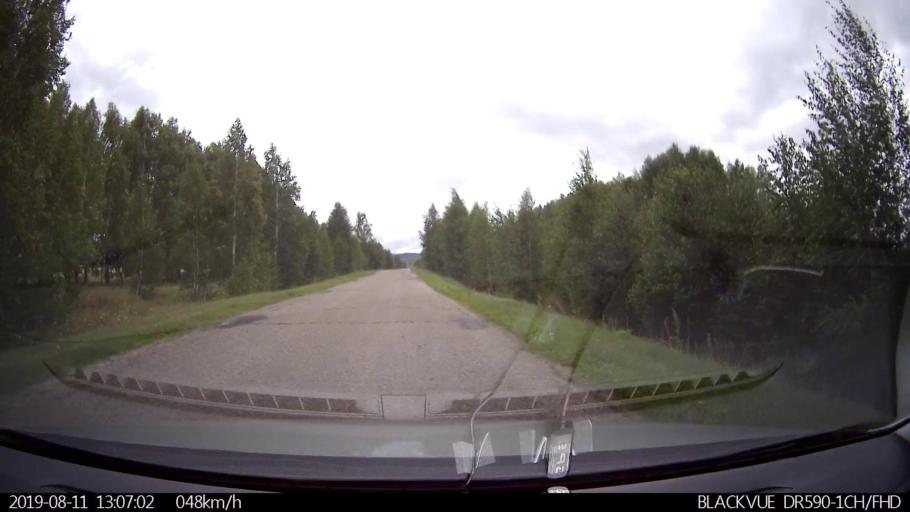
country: RU
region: Ulyanovsk
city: Ignatovka
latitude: 53.8656
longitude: 47.6395
